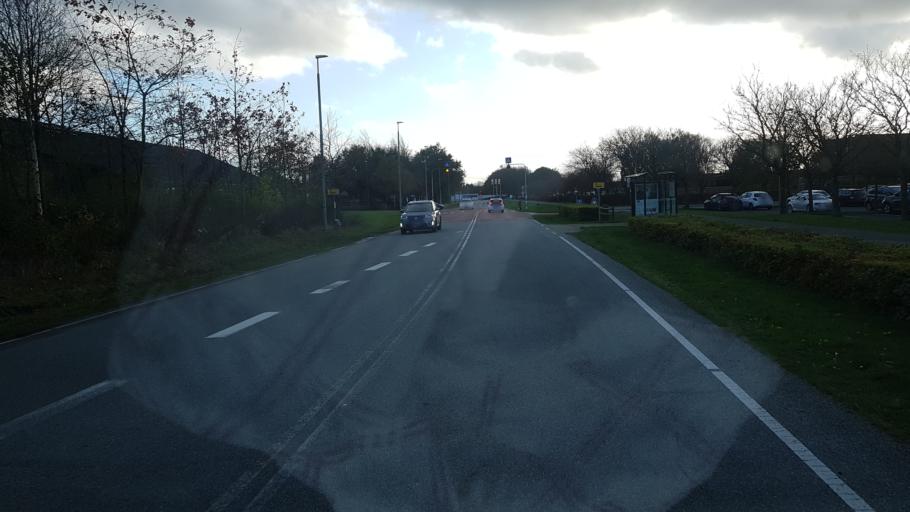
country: DK
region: South Denmark
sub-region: Billund Kommune
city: Grindsted
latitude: 55.7641
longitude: 8.9160
